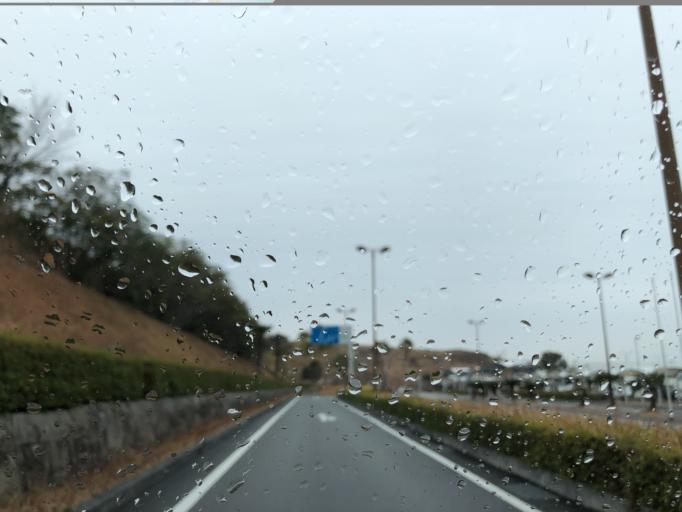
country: JP
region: Wakayama
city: Tanabe
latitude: 33.6619
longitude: 135.3602
